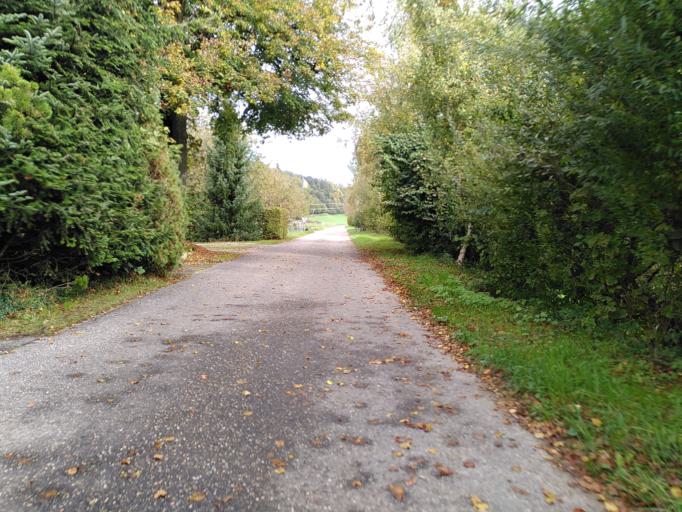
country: CH
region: Bern
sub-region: Emmental District
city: Wynigen
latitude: 47.1096
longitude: 7.6665
